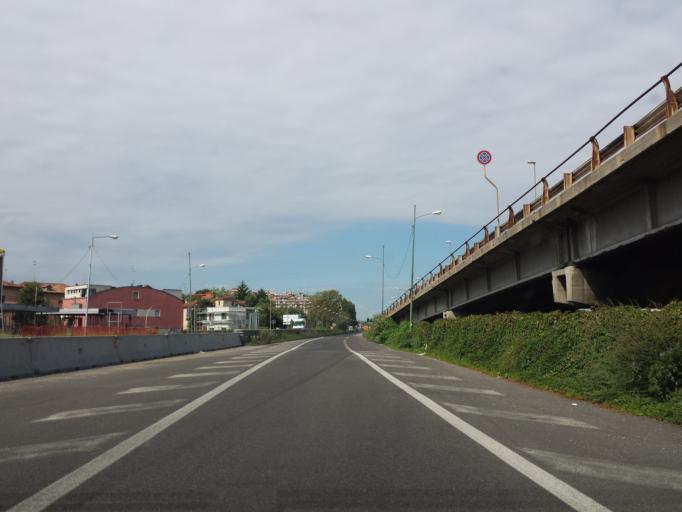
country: IT
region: Veneto
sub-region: Provincia di Venezia
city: Mestre
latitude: 45.4806
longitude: 12.2340
